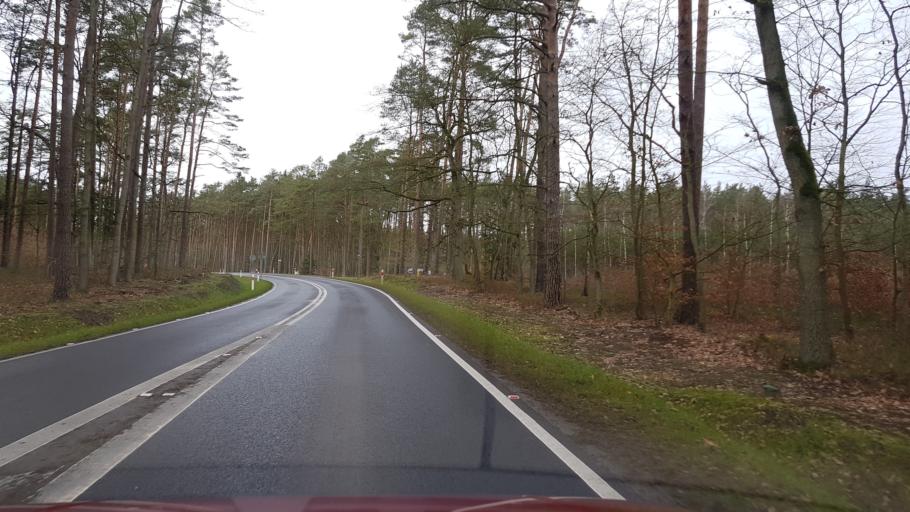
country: PL
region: West Pomeranian Voivodeship
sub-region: Powiat policki
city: Police
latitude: 53.6545
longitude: 14.4794
